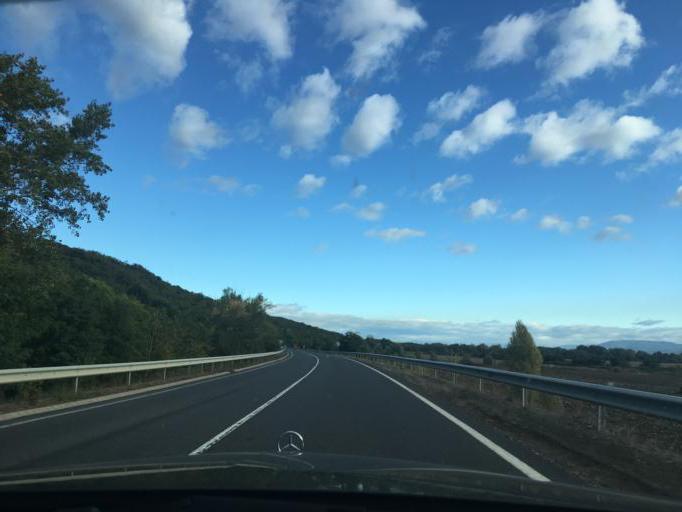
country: HU
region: Borsod-Abauj-Zemplen
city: Gonc
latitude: 48.4620
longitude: 21.1968
